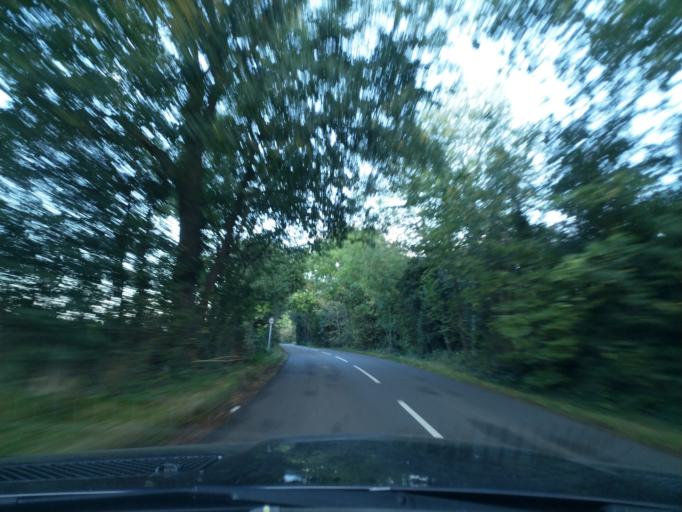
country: GB
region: England
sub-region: Warwickshire
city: Wroxall
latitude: 52.3483
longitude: -1.7065
